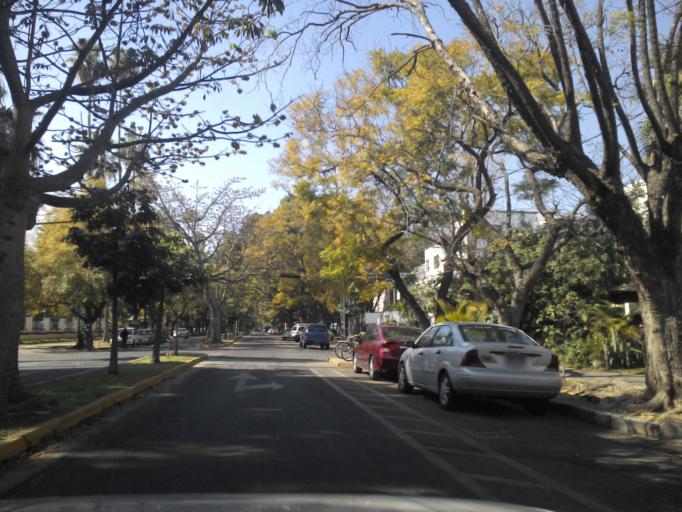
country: MX
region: Jalisco
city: Guadalajara
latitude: 20.6720
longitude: -103.3625
